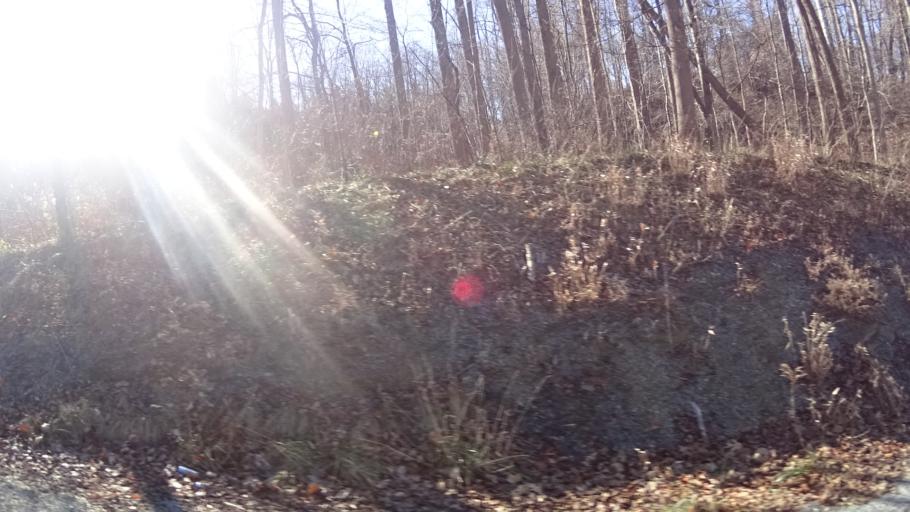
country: US
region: Ohio
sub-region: Huron County
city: Wakeman
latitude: 41.3030
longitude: -82.3440
